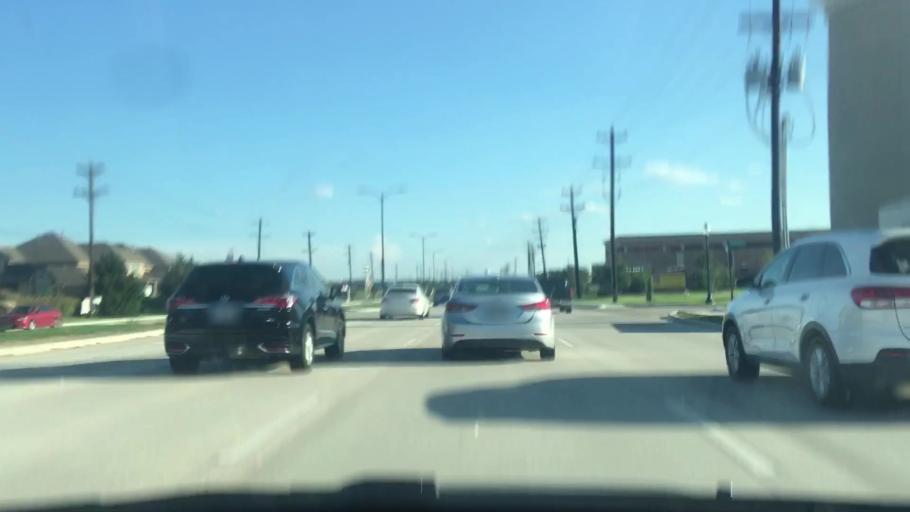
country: US
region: Texas
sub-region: Denton County
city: Little Elm
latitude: 33.1874
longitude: -96.8872
